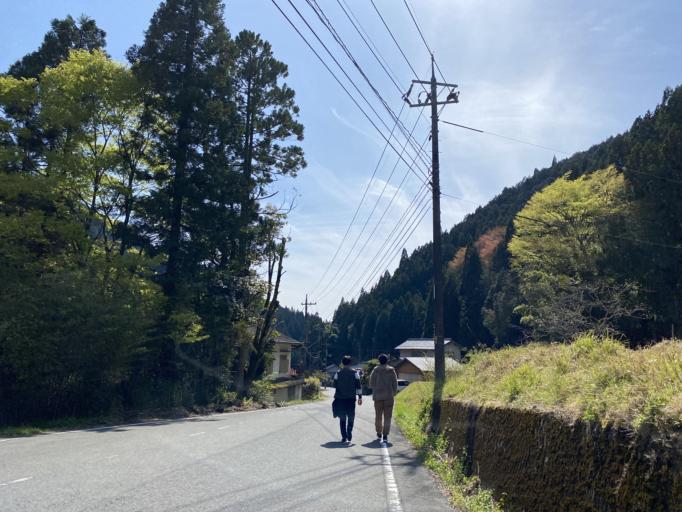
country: JP
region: Hyogo
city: Yamazakicho-nakabirose
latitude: 35.1693
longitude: 134.3475
